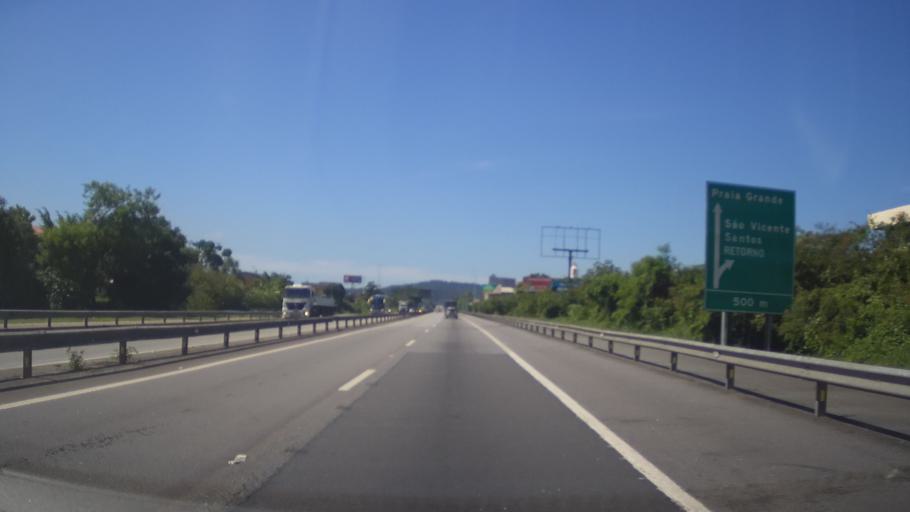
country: BR
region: Sao Paulo
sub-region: Sao Vicente
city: Sao Vicente
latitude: -23.9442
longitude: -46.4183
